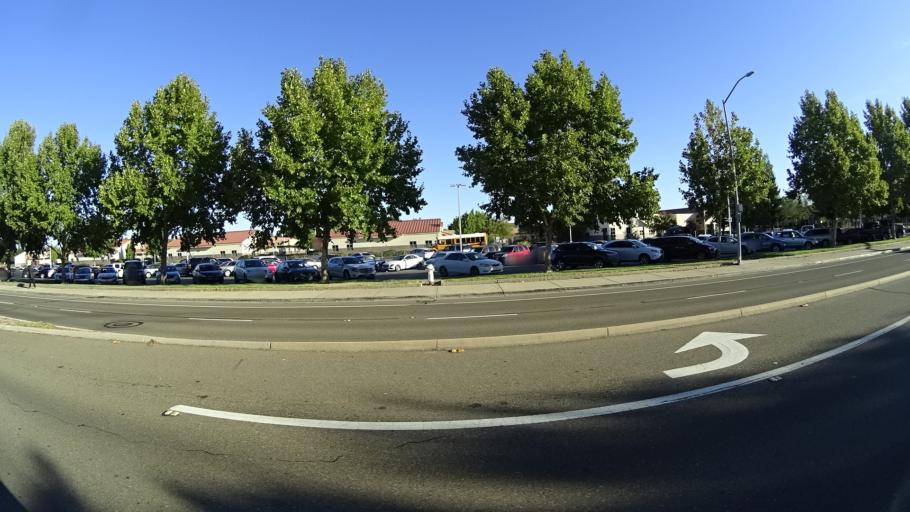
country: US
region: California
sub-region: Sacramento County
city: Laguna
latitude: 38.4480
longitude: -121.3976
